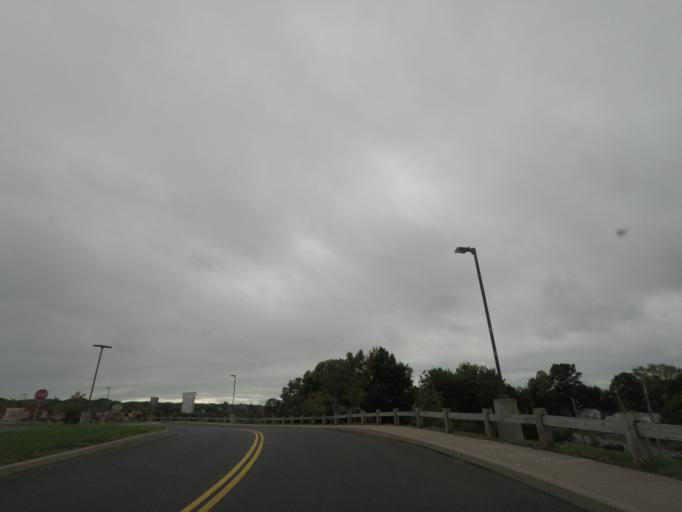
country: US
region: New York
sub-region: Albany County
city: Menands
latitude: 42.6568
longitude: -73.6925
